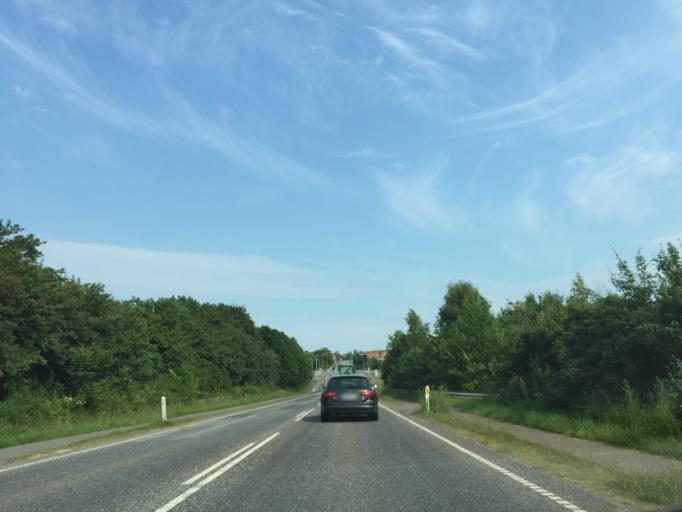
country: DK
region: Central Jutland
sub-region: Syddjurs Kommune
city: Ronde
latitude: 56.3040
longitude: 10.4601
